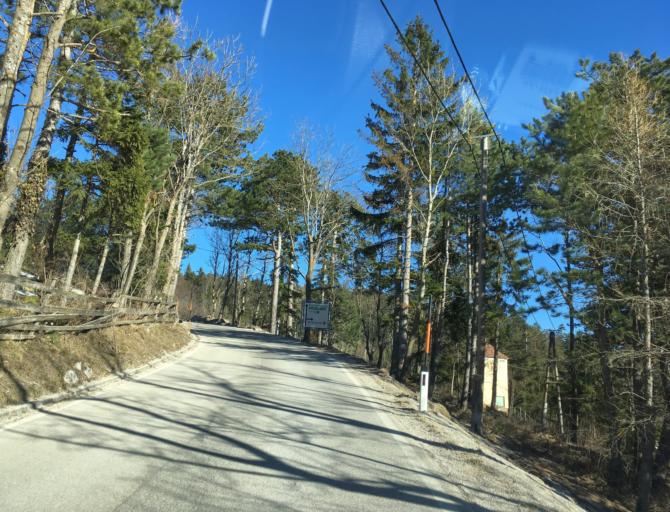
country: AT
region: Lower Austria
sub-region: Politischer Bezirk Wiener Neustadt
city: Waldegg
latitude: 47.8395
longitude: 16.0579
